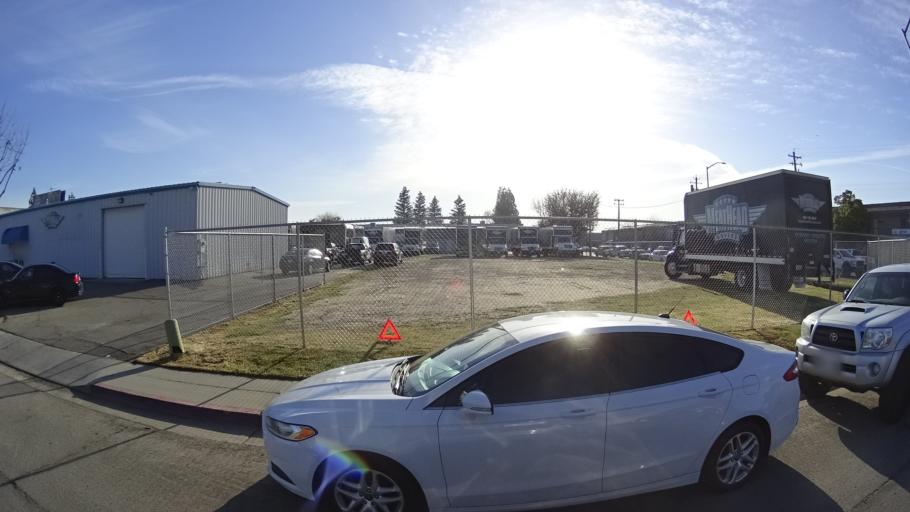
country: US
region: California
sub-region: Fresno County
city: West Park
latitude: 36.8071
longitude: -119.8685
